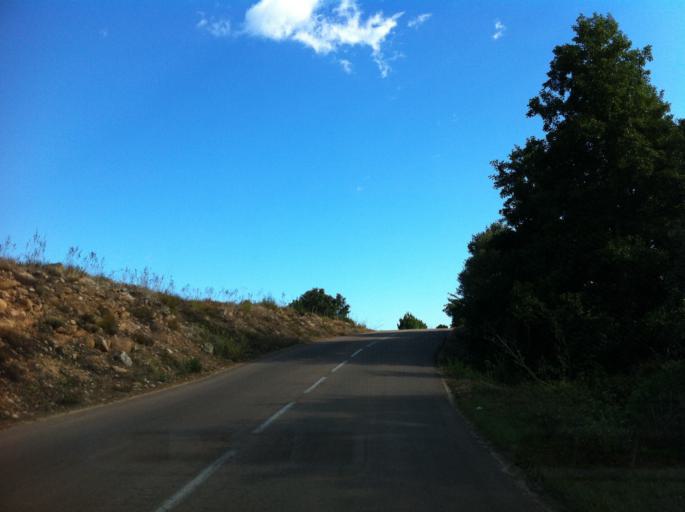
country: FR
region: Corsica
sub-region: Departement de la Corse-du-Sud
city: Porto-Vecchio
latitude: 41.6406
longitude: 9.2948
